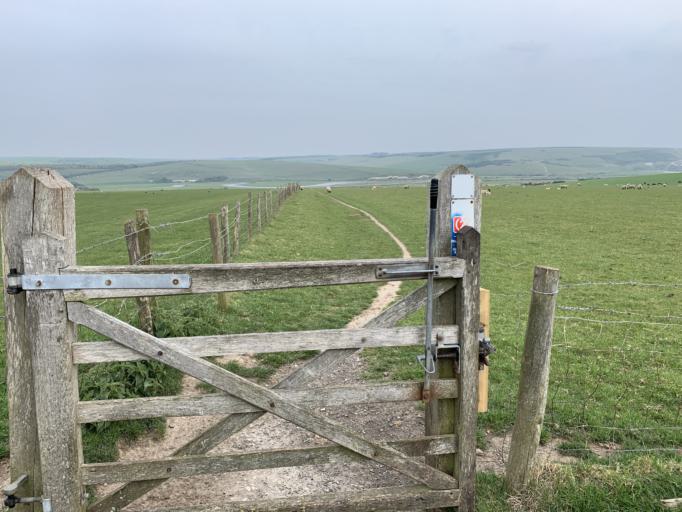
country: GB
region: England
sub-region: East Sussex
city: Seaford
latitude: 50.7717
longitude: 0.1349
